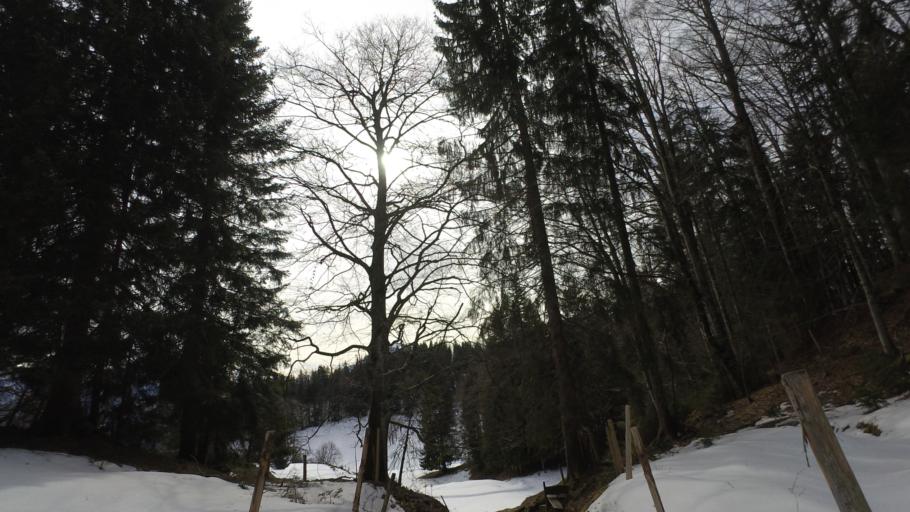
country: DE
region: Bavaria
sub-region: Upper Bavaria
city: Reit im Winkl
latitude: 47.6885
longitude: 12.4451
